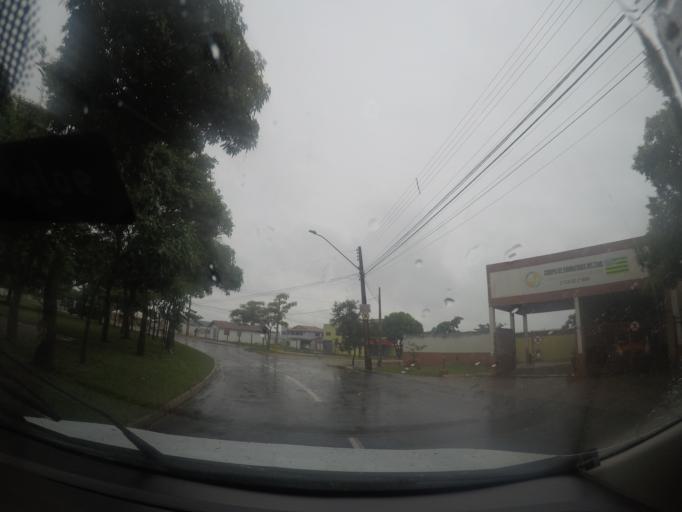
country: BR
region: Goias
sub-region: Goiania
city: Goiania
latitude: -16.6056
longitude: -49.3363
